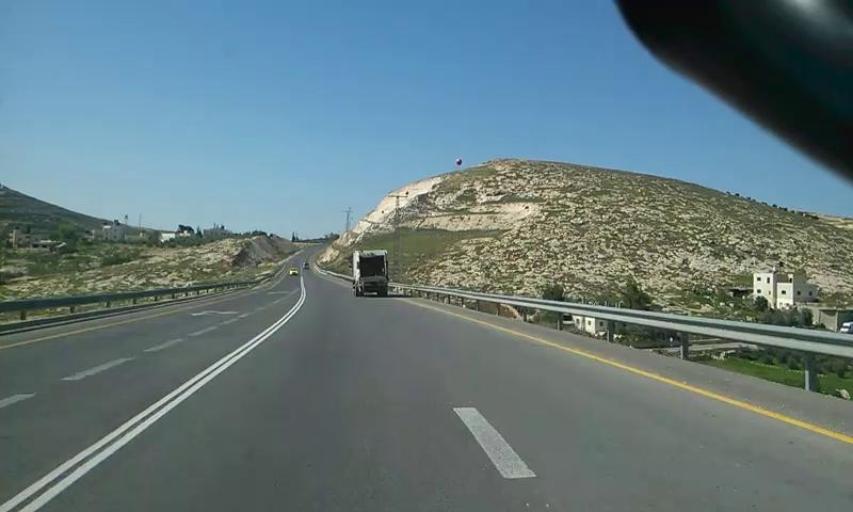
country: PS
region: West Bank
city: Bayt Ta`mar
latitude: 31.6692
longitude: 35.2381
